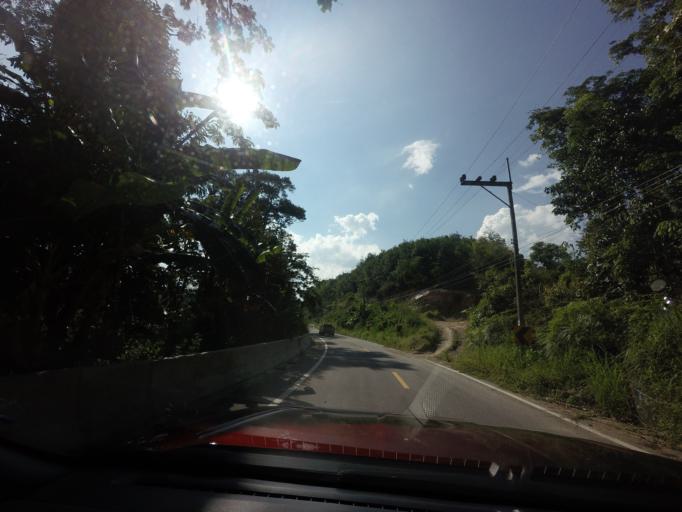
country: TH
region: Yala
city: Than To
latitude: 6.0776
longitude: 101.3350
